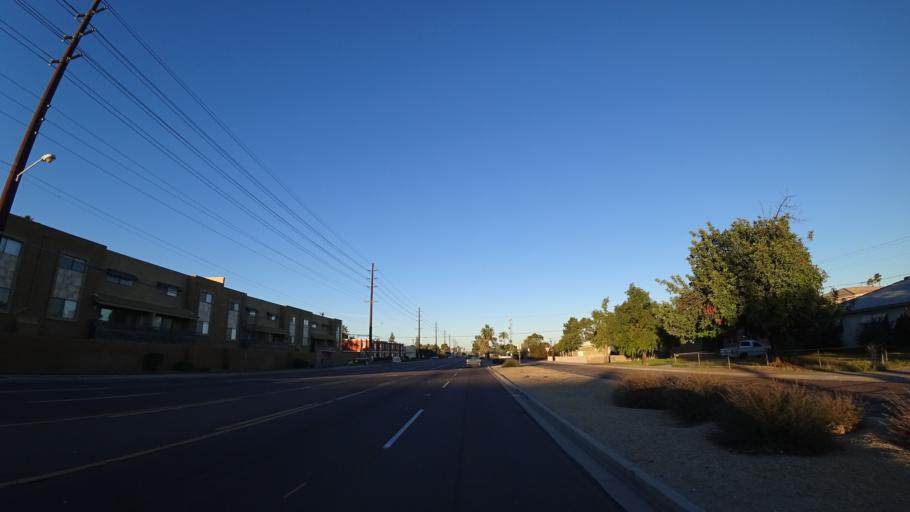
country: US
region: Arizona
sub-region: Maricopa County
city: Paradise Valley
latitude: 33.4801
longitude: -111.9642
